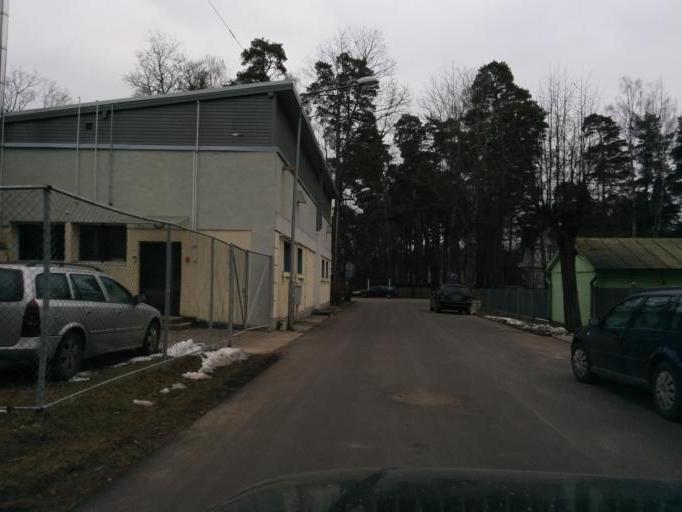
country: LV
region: Babite
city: Pinki
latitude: 56.9836
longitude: 23.8537
